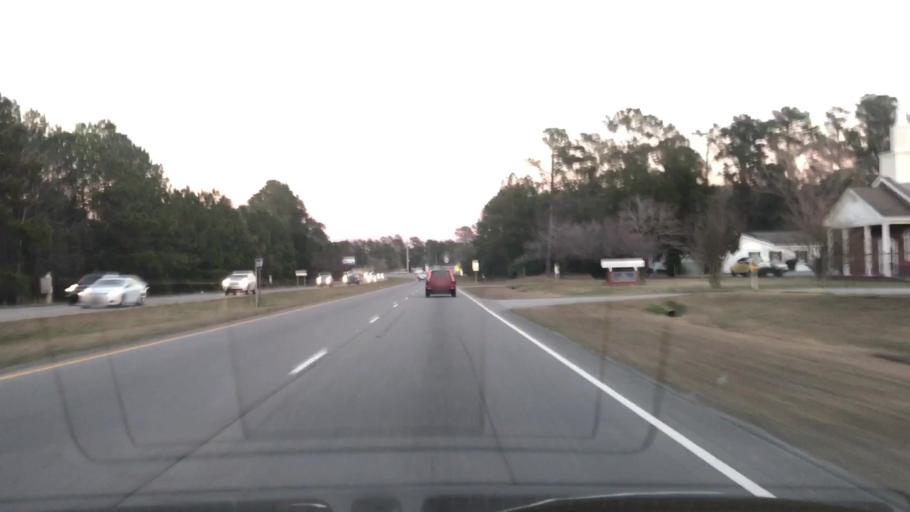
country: US
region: North Carolina
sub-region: Brunswick County
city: Shallotte
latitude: 34.0181
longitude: -78.2707
